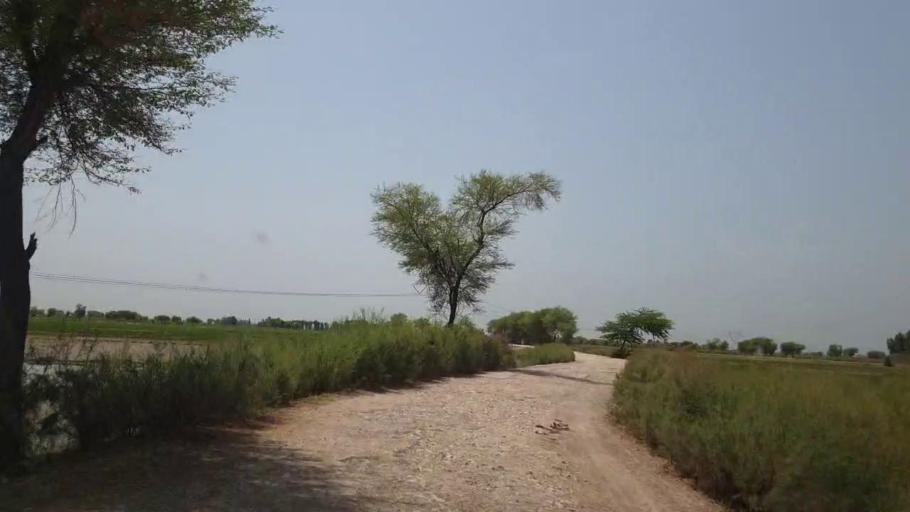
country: PK
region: Sindh
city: Shikarpur
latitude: 27.8910
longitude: 68.6309
